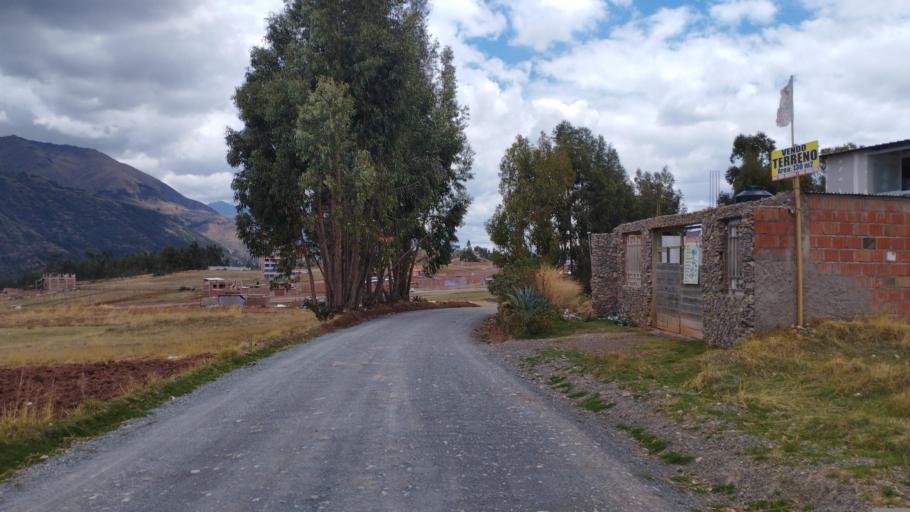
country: PE
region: Cusco
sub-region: Provincia de Cusco
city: Cusco
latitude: -13.5123
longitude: -71.9378
